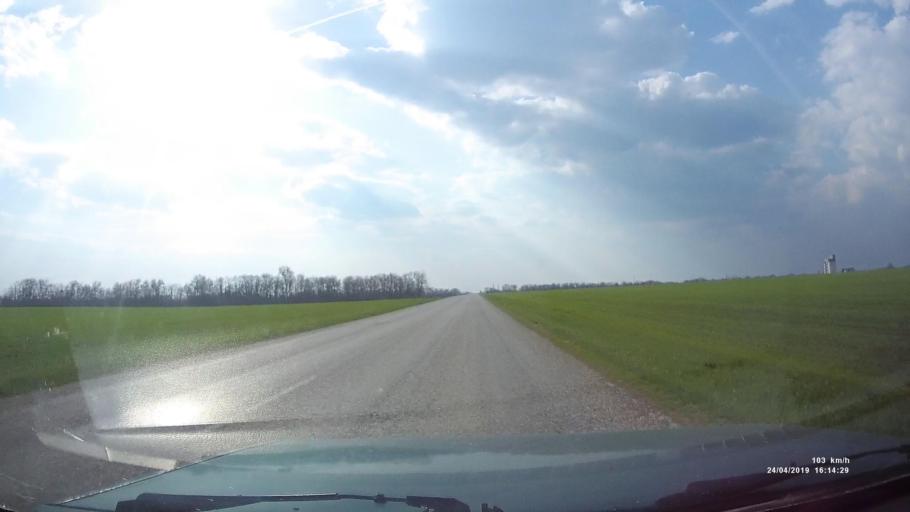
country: RU
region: Rostov
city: Sovetskoye
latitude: 46.7530
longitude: 42.1981
